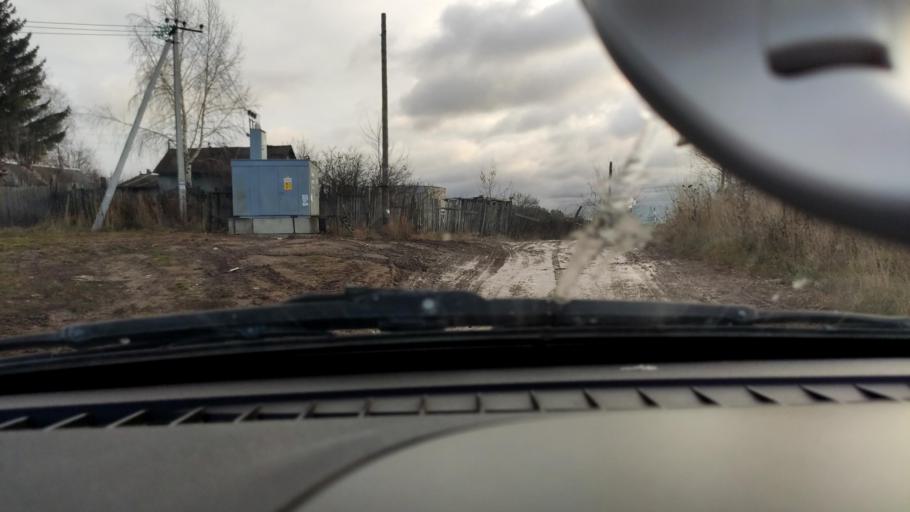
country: RU
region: Perm
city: Kondratovo
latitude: 57.9554
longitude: 56.1470
